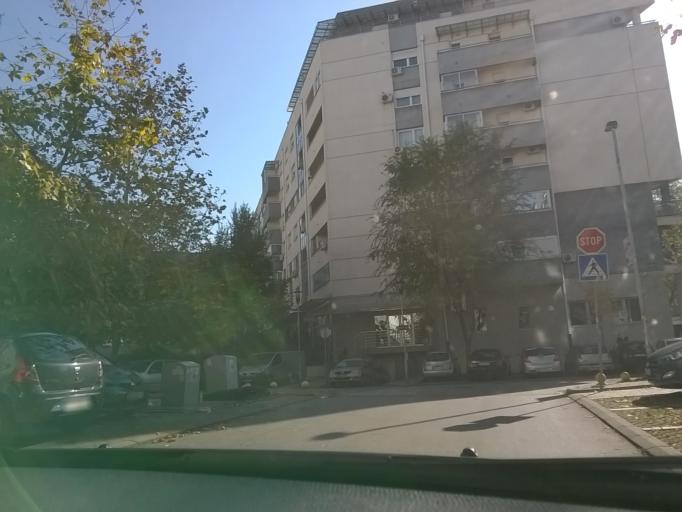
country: RS
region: Central Serbia
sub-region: Belgrade
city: Novi Beograd
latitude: 44.8123
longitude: 20.4253
